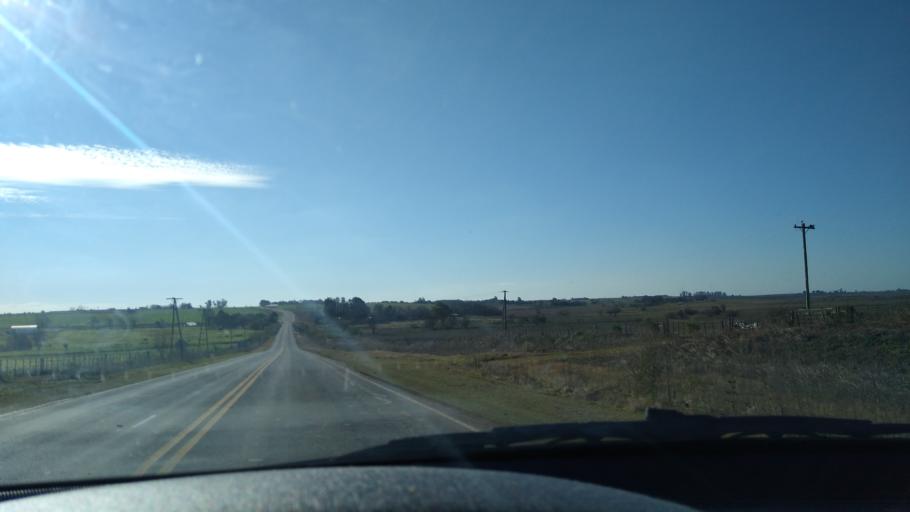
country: AR
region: Entre Rios
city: Aranguren
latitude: -32.4089
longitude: -60.3226
